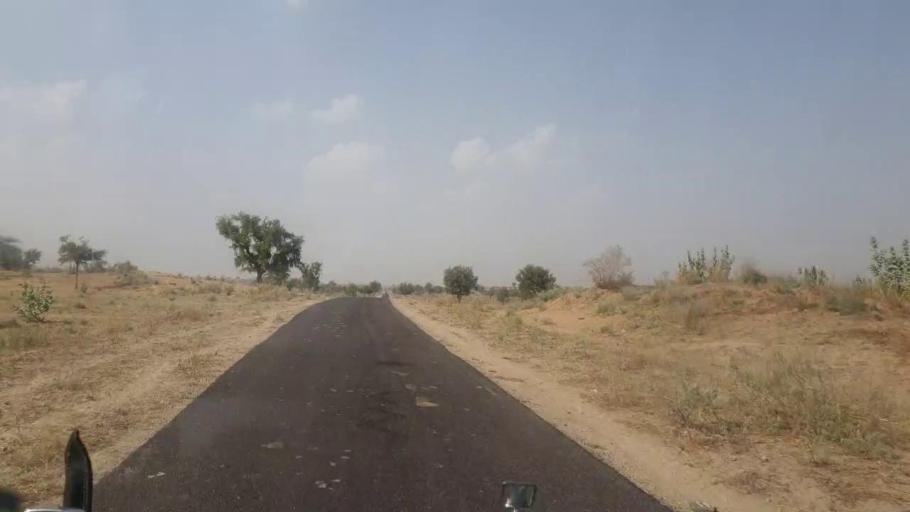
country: PK
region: Sindh
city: Islamkot
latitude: 25.1791
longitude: 70.2874
